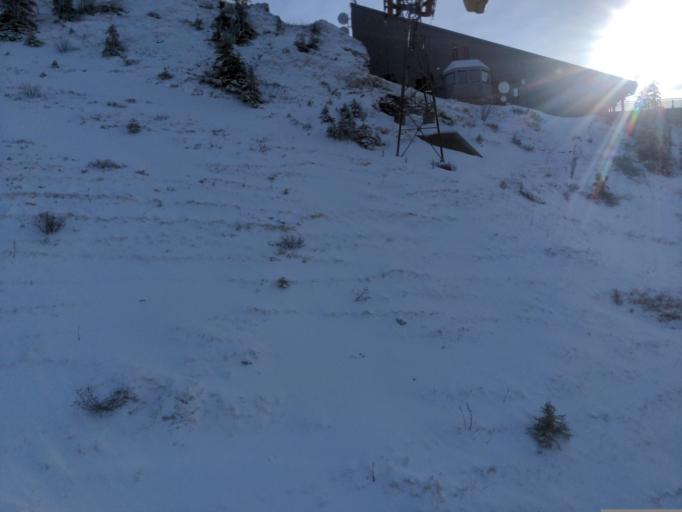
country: DE
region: Bavaria
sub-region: Swabia
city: Balderschwang
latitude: 47.4932
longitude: 10.0718
